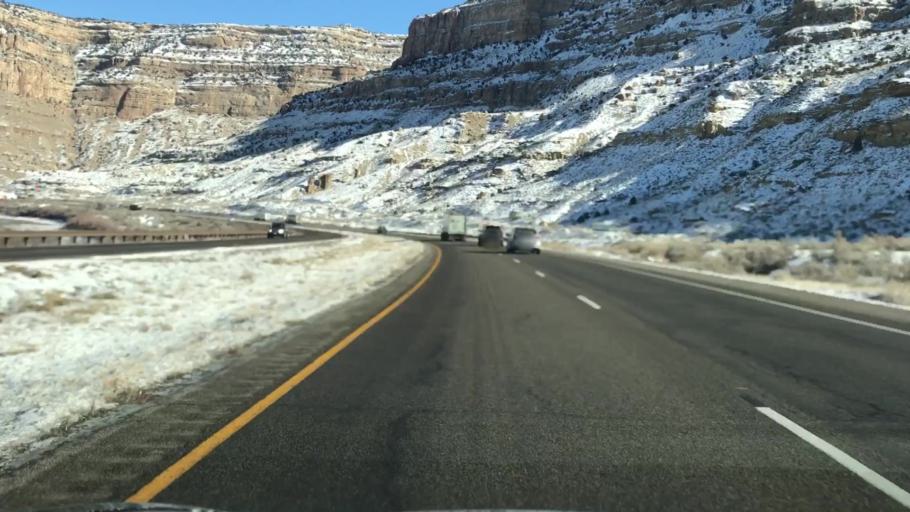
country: US
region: Colorado
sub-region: Mesa County
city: Palisade
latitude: 39.1508
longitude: -108.3057
